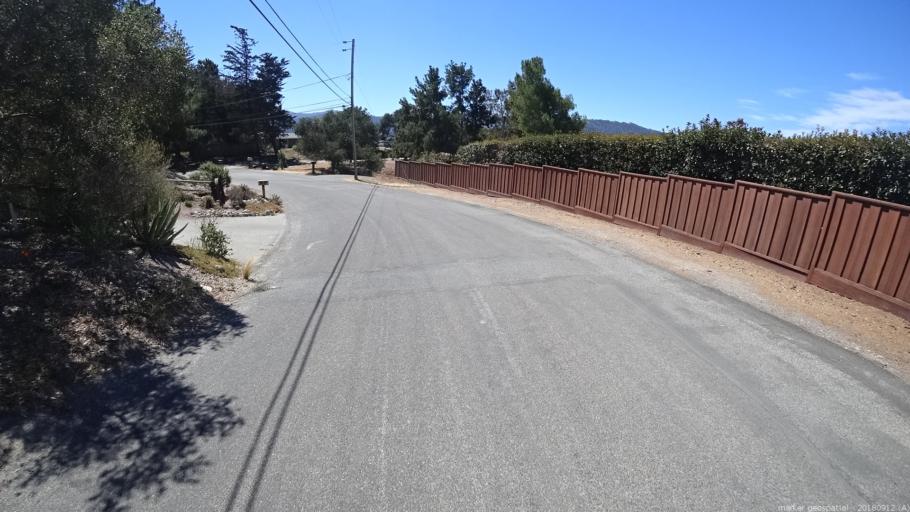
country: US
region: California
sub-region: Monterey County
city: Carmel Valley Village
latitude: 36.4904
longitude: -121.7211
